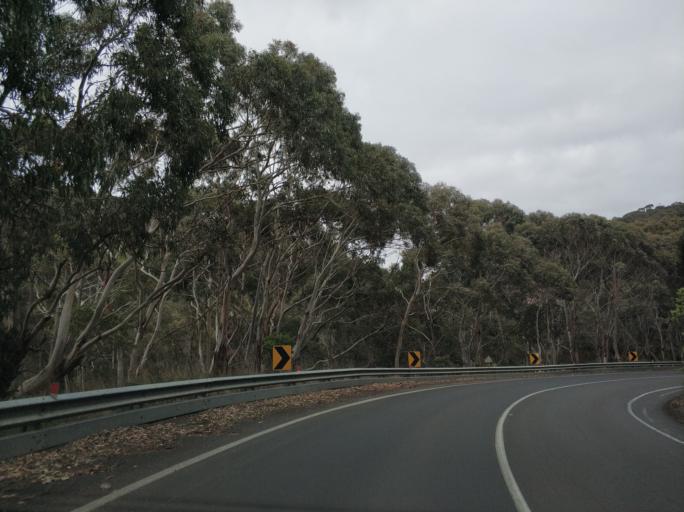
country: AU
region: Victoria
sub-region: Surf Coast
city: Anglesea
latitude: -38.4821
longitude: 144.0286
